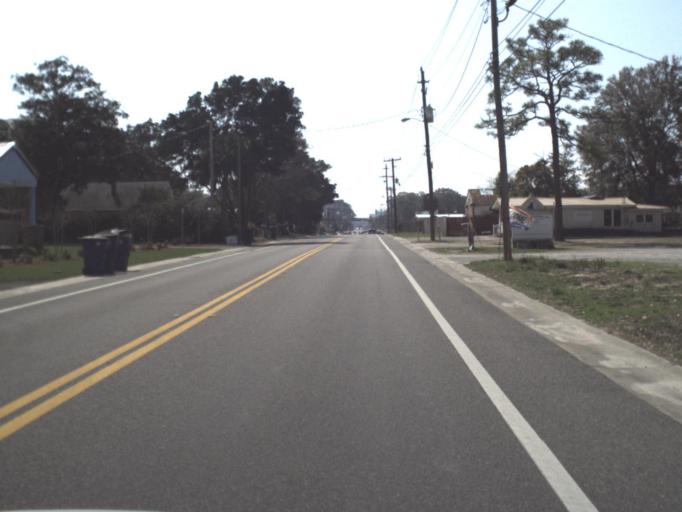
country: US
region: Florida
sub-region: Bay County
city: Pretty Bayou
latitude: 30.1807
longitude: -85.7014
